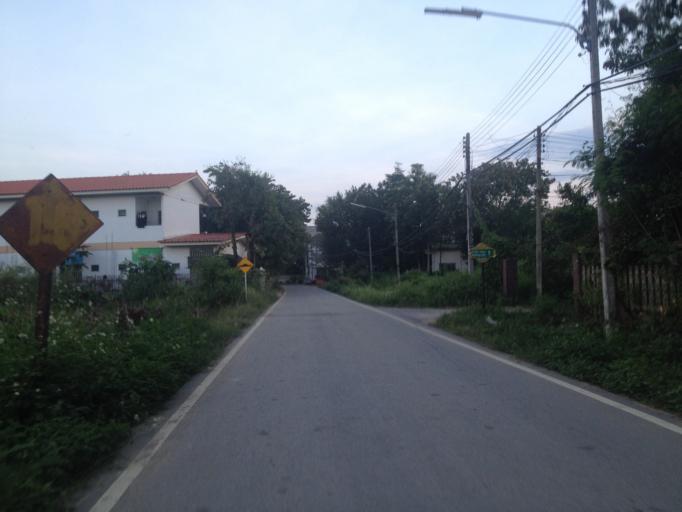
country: TH
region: Chiang Mai
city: Chiang Mai
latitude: 18.7531
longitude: 98.9555
